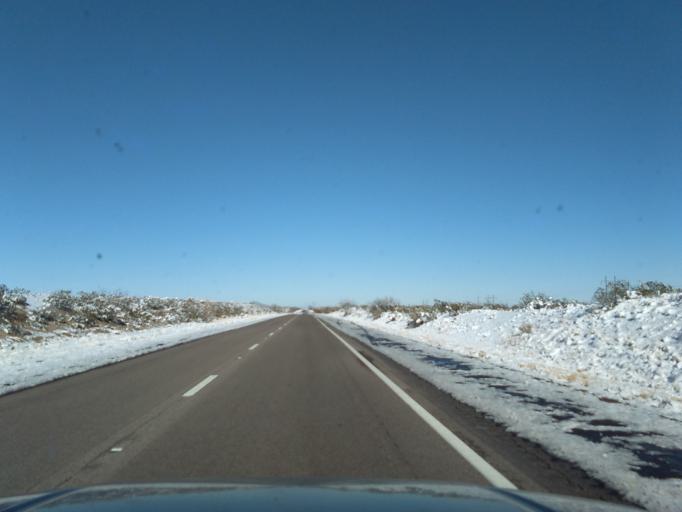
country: US
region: New Mexico
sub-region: Socorro County
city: Socorro
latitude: 33.6681
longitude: -107.0835
